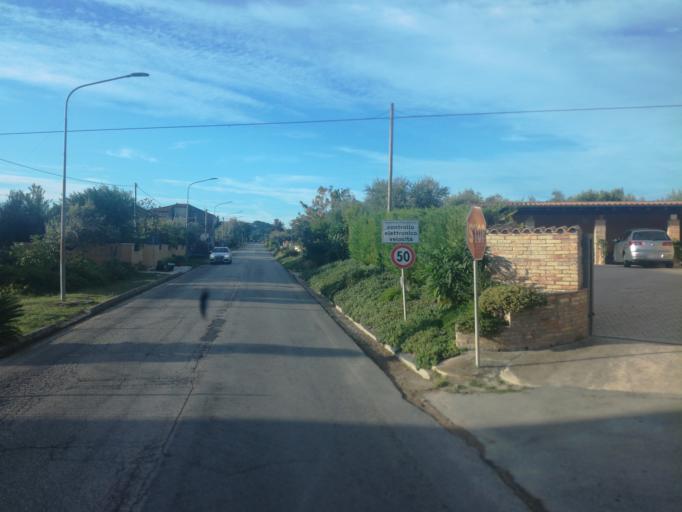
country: IT
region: Abruzzo
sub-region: Provincia di Chieti
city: Miglianico
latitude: 42.3802
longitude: 14.2897
